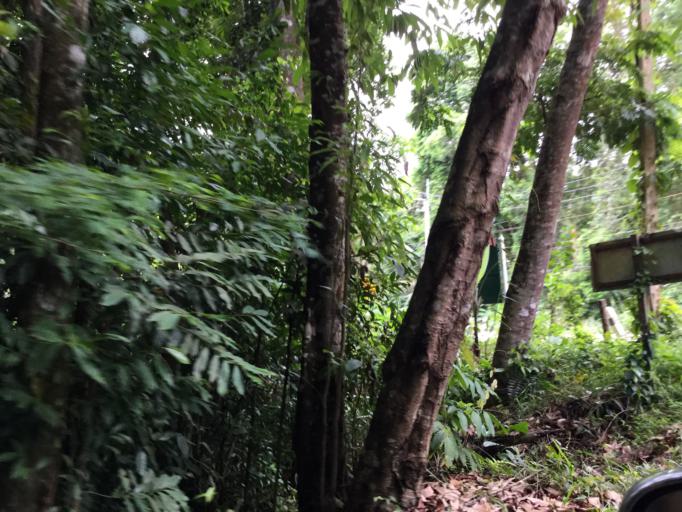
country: TH
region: Nakhon Si Thammarat
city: Ko Pha Ngan
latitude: 9.7294
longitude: 100.0467
